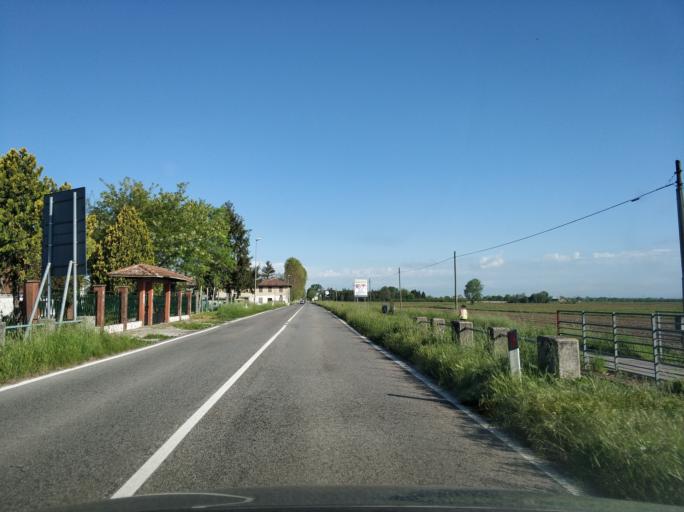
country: IT
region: Friuli Venezia Giulia
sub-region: Provincia di Udine
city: Aquileia
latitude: 45.7804
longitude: 13.3622
